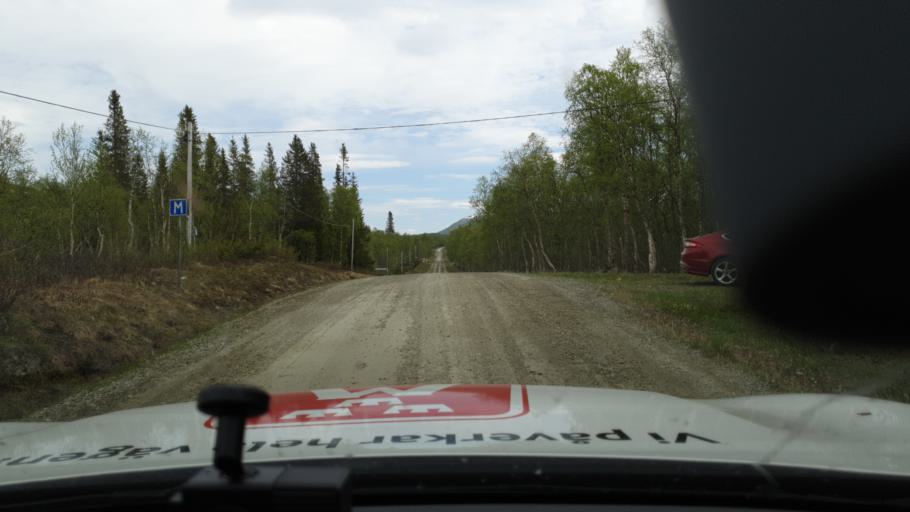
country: NO
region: Nordland
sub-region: Rana
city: Mo i Rana
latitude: 65.7590
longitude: 15.2995
